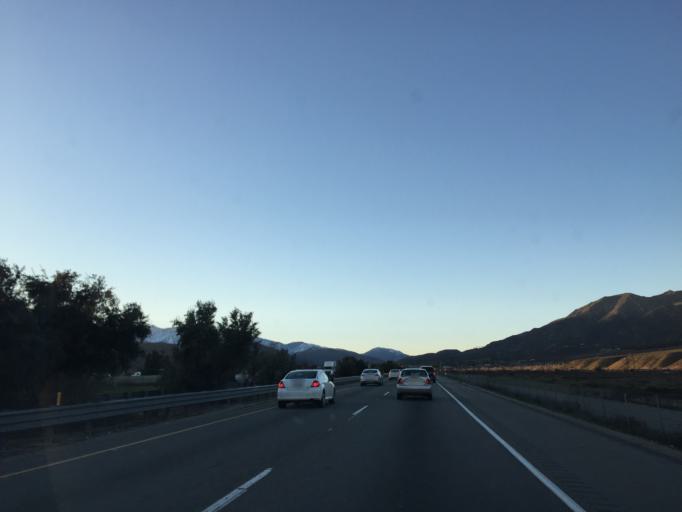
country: US
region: California
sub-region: San Bernardino County
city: Muscoy
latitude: 34.2031
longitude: -117.3769
